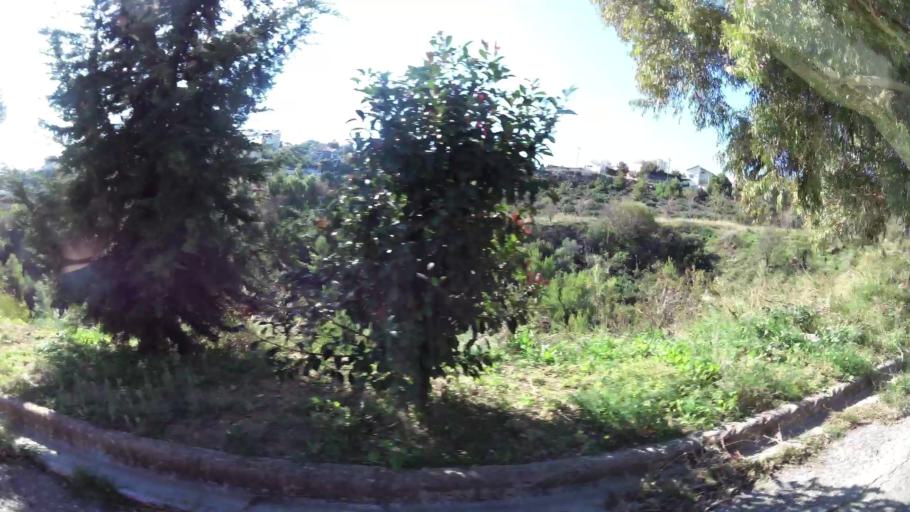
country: GR
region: Attica
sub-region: Nomarchia Anatolikis Attikis
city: Dhrafi
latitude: 38.0310
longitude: 23.8969
